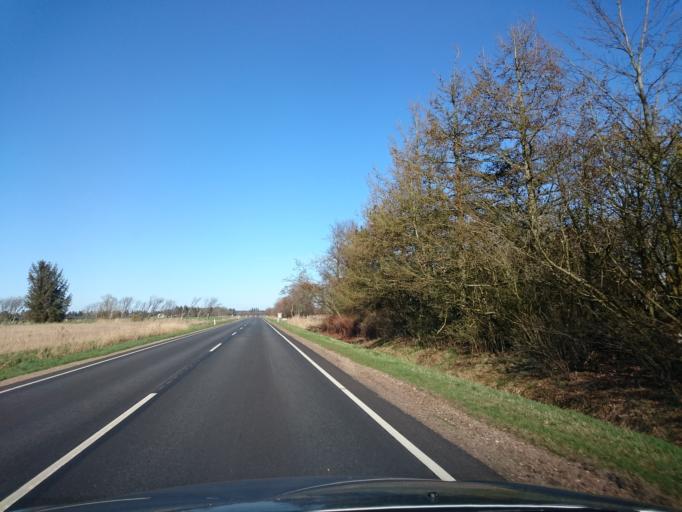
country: DK
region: North Denmark
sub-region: Hjorring Kommune
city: Sindal
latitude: 57.5956
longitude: 10.3046
